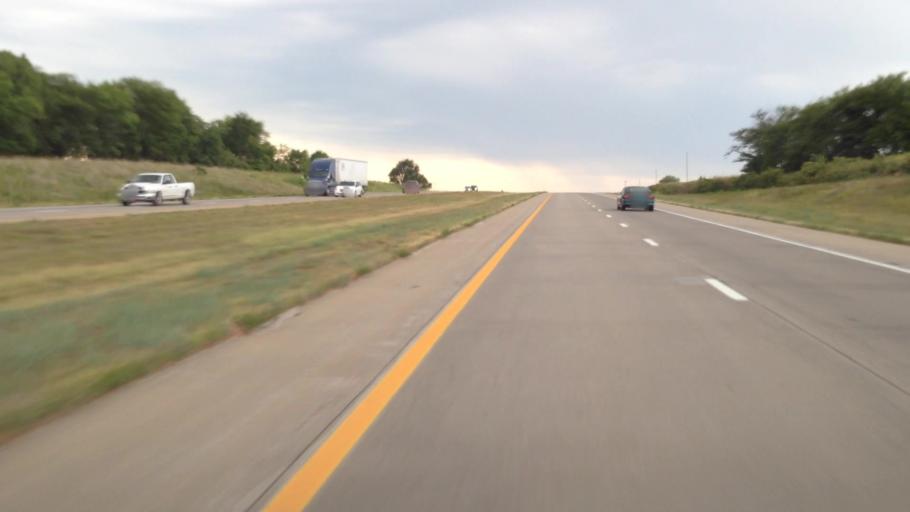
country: US
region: Kansas
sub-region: Osage County
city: Lyndon
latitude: 38.4790
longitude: -95.5033
